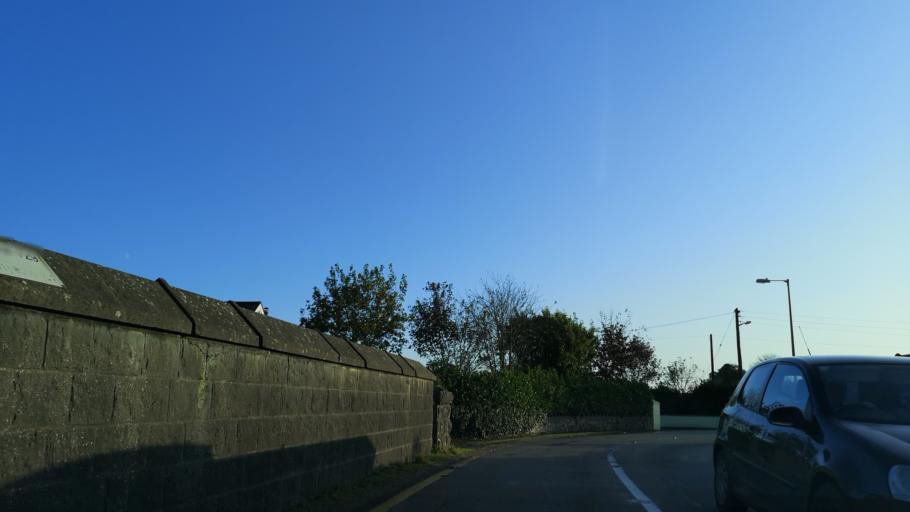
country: IE
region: Connaught
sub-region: Roscommon
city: Castlerea
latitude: 53.7651
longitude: -8.5039
